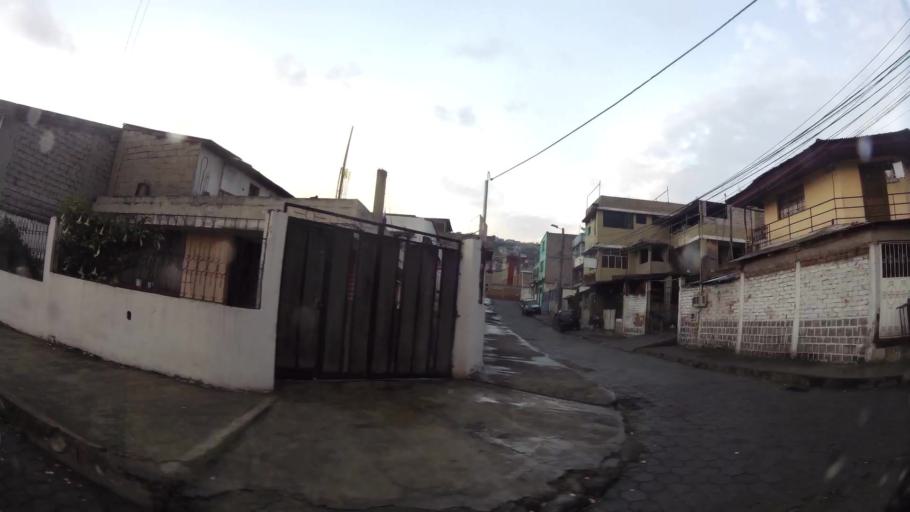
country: EC
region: Pichincha
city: Quito
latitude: -0.2956
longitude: -78.5386
